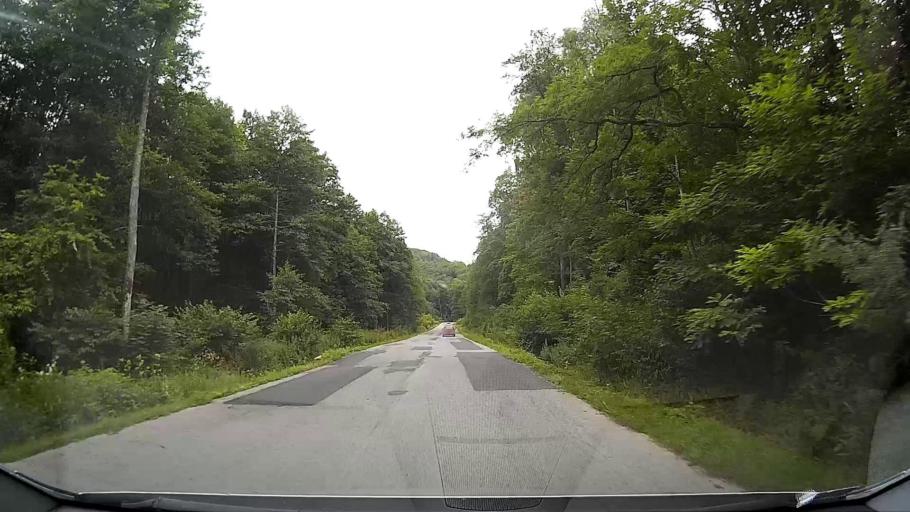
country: SK
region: Banskobystricky
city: Tisovec
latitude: 48.7125
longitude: 20.0008
